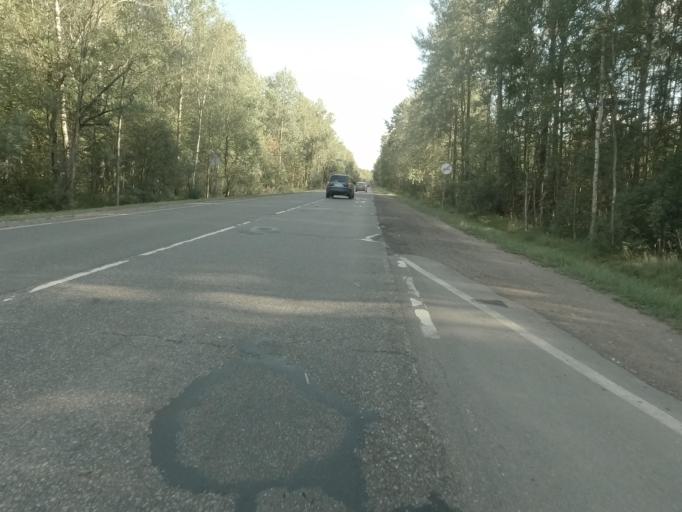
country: RU
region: Leningrad
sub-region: Volosovskiy Rayon
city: Shlissel'burg
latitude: 59.9374
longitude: 30.9825
